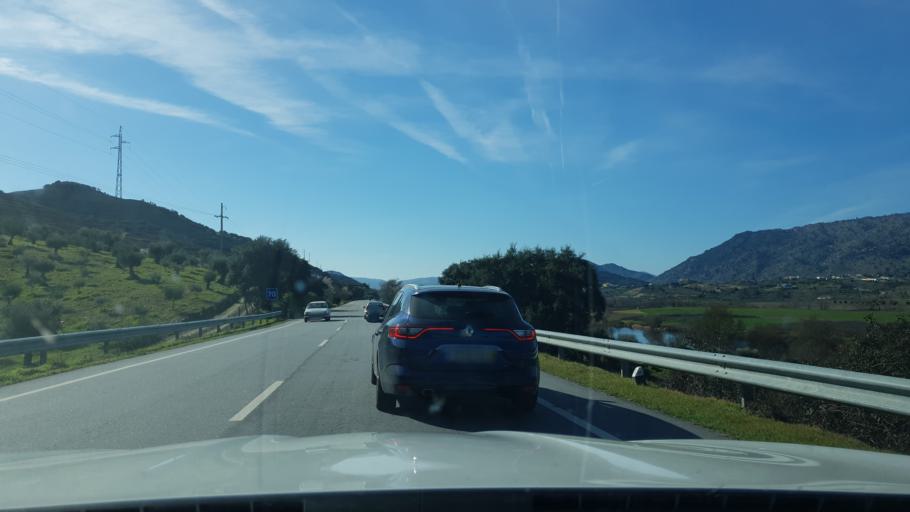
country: PT
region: Braganca
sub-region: Torre de Moncorvo
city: Torre de Moncorvo
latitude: 41.1966
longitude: -7.0963
